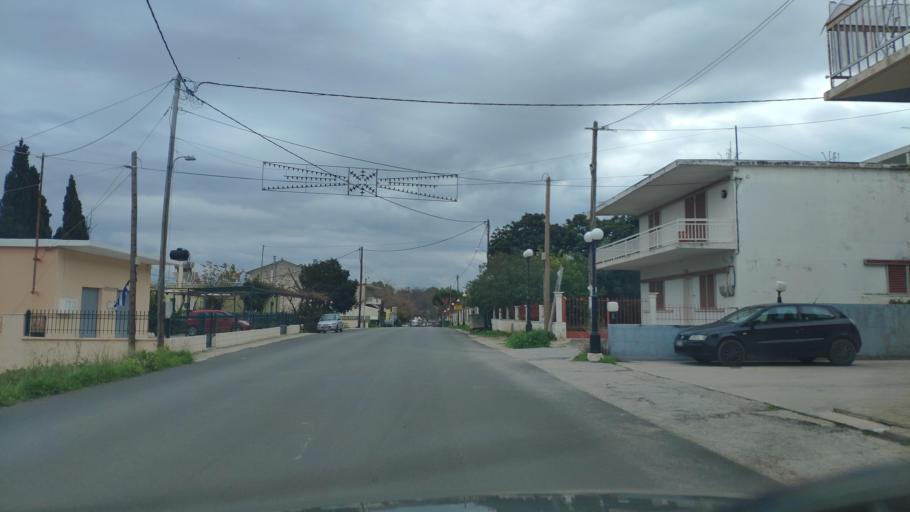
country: GR
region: Peloponnese
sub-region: Nomos Argolidos
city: Nea Kios
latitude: 37.5555
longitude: 22.7153
